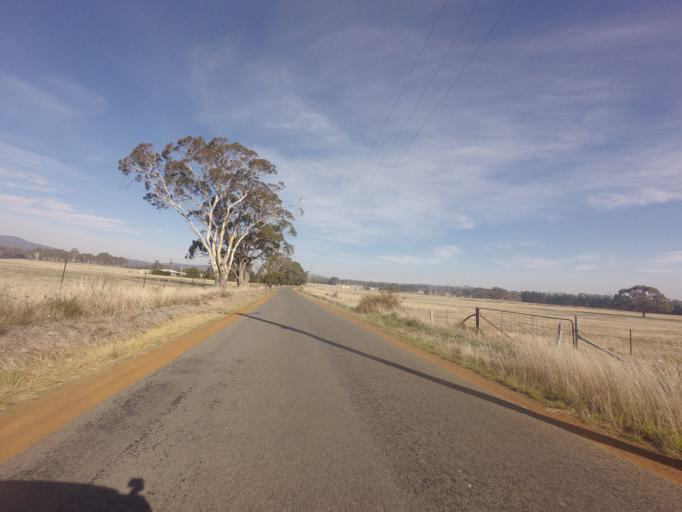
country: AU
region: Tasmania
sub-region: Sorell
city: Sorell
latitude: -42.4364
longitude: 147.4722
